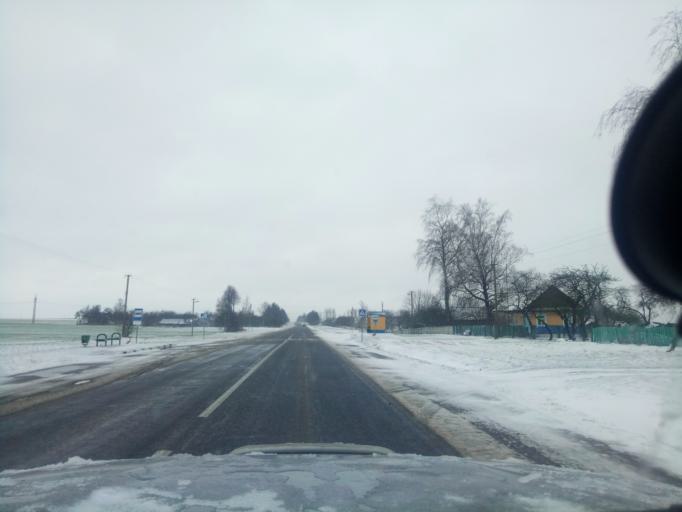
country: BY
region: Minsk
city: Klyetsk
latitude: 53.1152
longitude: 26.6620
